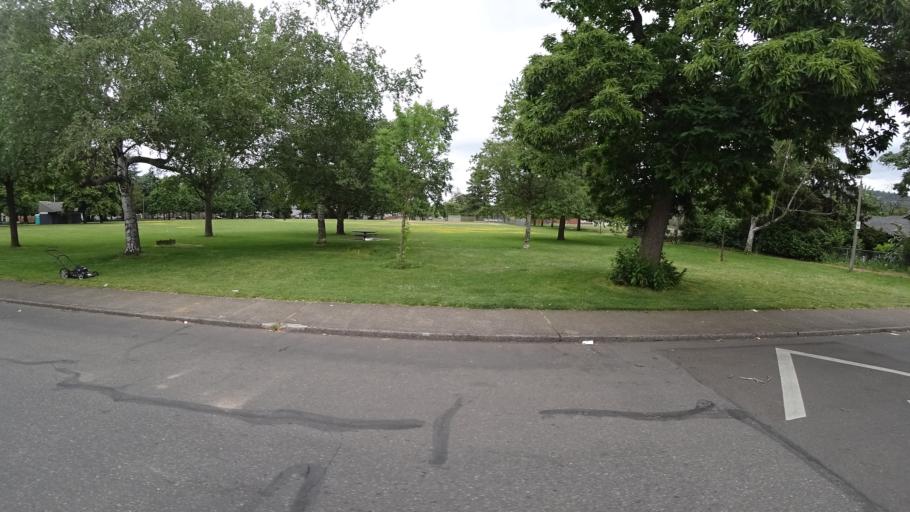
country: US
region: Oregon
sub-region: Multnomah County
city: Lents
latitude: 45.4734
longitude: -122.5739
